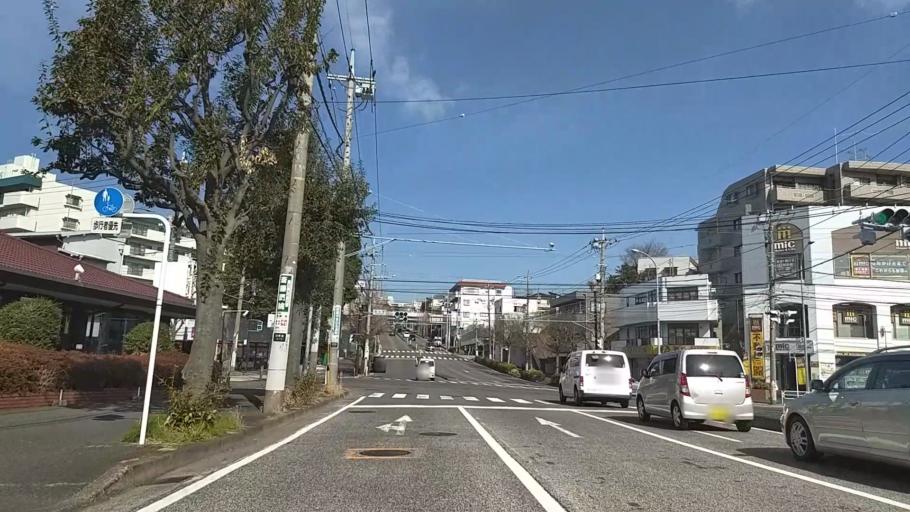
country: JP
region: Kanagawa
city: Kamakura
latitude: 35.3825
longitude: 139.5774
